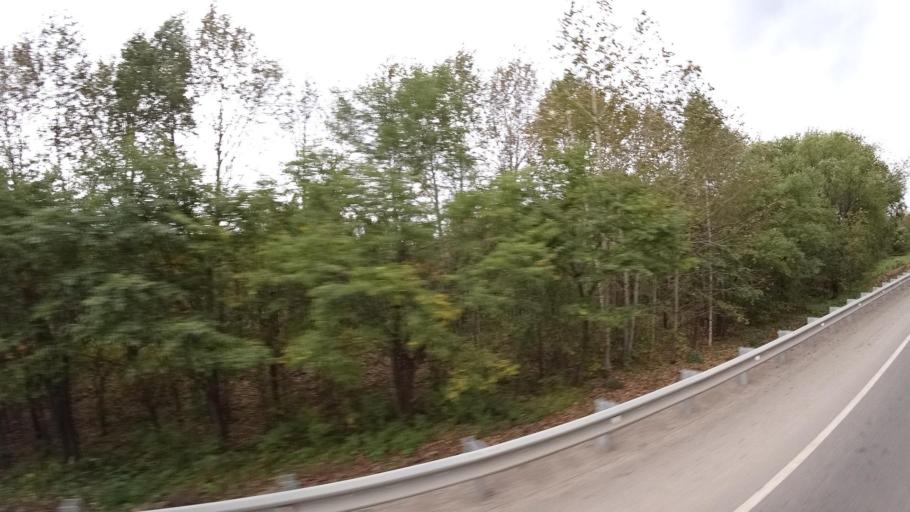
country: RU
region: Jewish Autonomous Oblast
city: Khingansk
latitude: 48.9893
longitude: 131.1269
